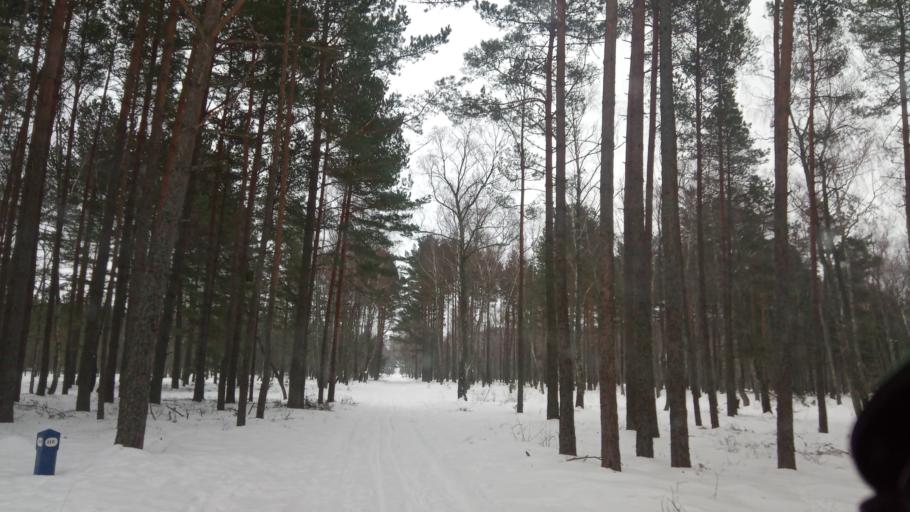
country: LT
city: Neringa
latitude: 55.4186
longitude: 21.0972
